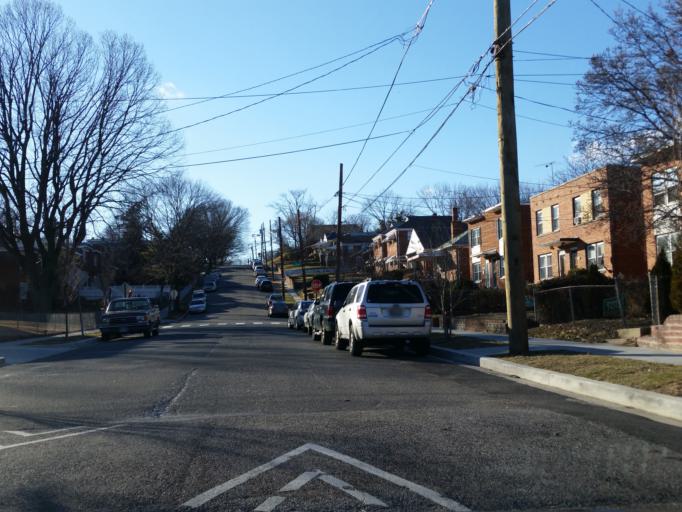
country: US
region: Maryland
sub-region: Prince George's County
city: Chillum
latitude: 38.9613
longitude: -77.0003
